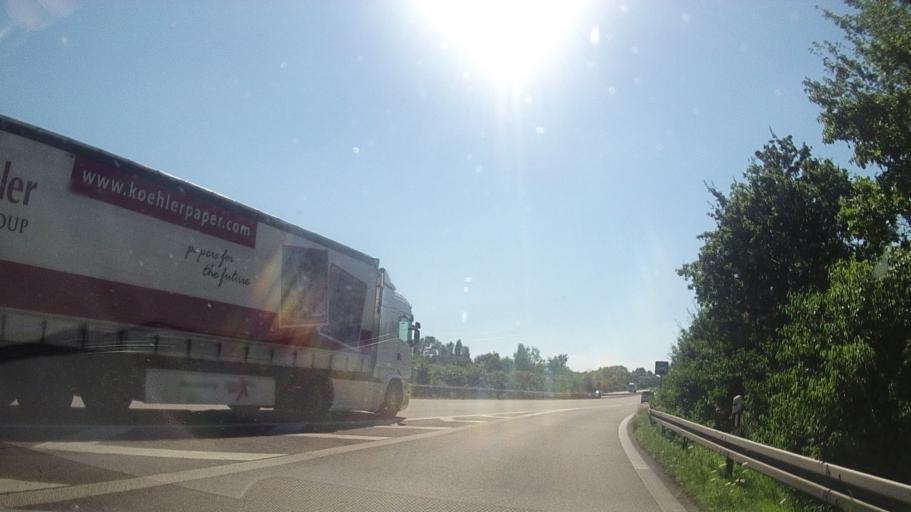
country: DE
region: Baden-Wuerttemberg
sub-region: Freiburg Region
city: Willstatt
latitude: 48.5349
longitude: 7.9308
